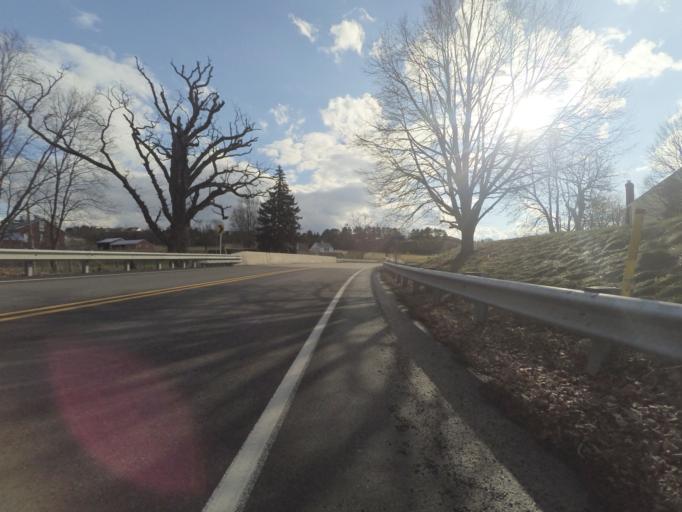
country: US
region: Pennsylvania
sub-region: Centre County
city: Lemont
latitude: 40.7912
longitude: -77.8324
